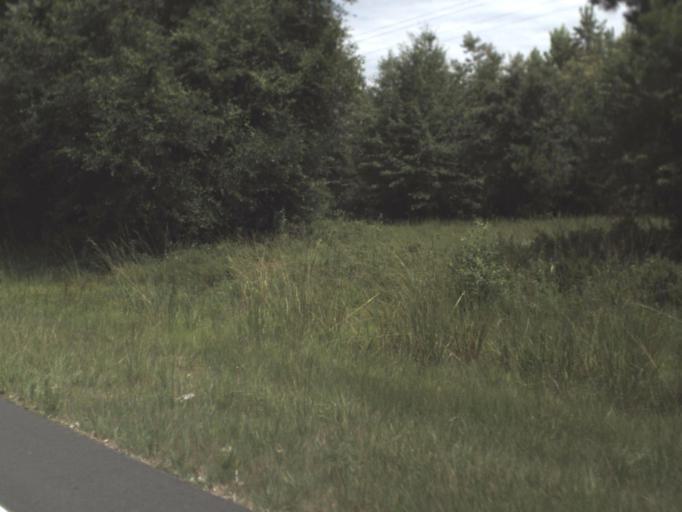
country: US
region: Florida
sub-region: Jefferson County
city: Monticello
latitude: 30.4756
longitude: -83.6679
